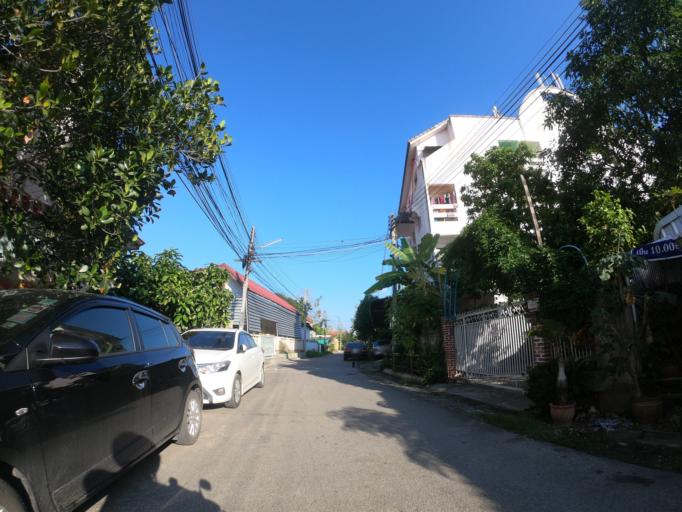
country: TH
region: Chiang Mai
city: Chiang Mai
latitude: 18.7545
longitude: 98.9696
